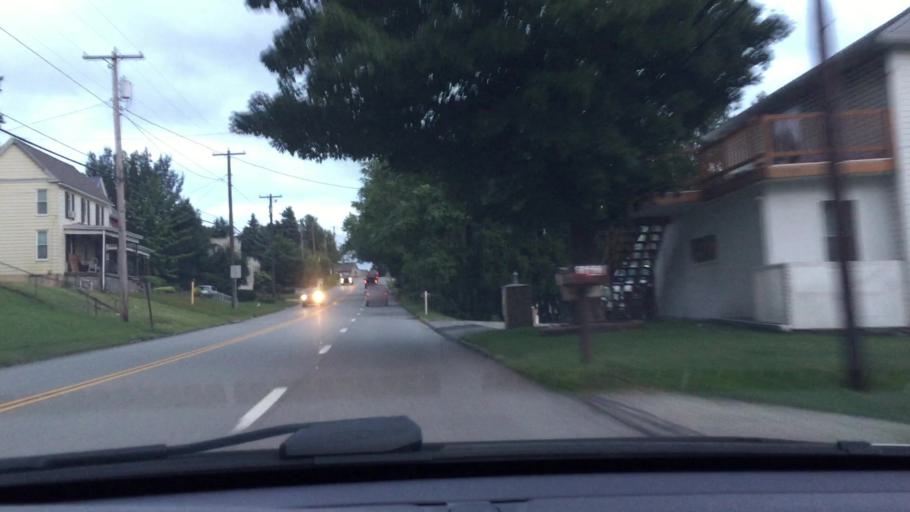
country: US
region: Pennsylvania
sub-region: Washington County
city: East Washington
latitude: 40.1566
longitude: -80.2163
